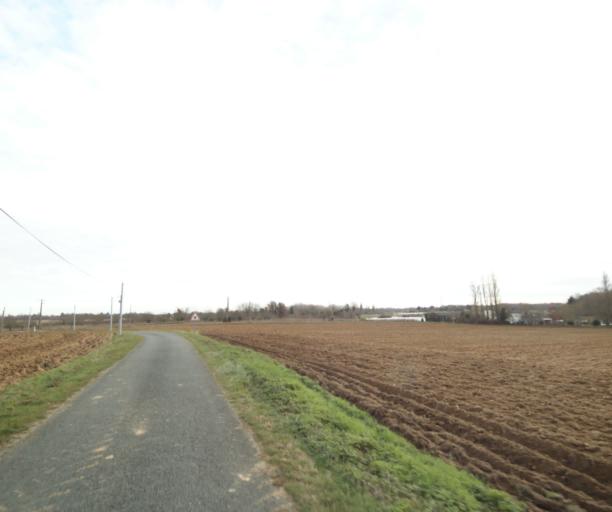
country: FR
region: Poitou-Charentes
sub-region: Departement de la Charente-Maritime
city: Corme-Royal
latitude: 45.7826
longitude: -0.8203
